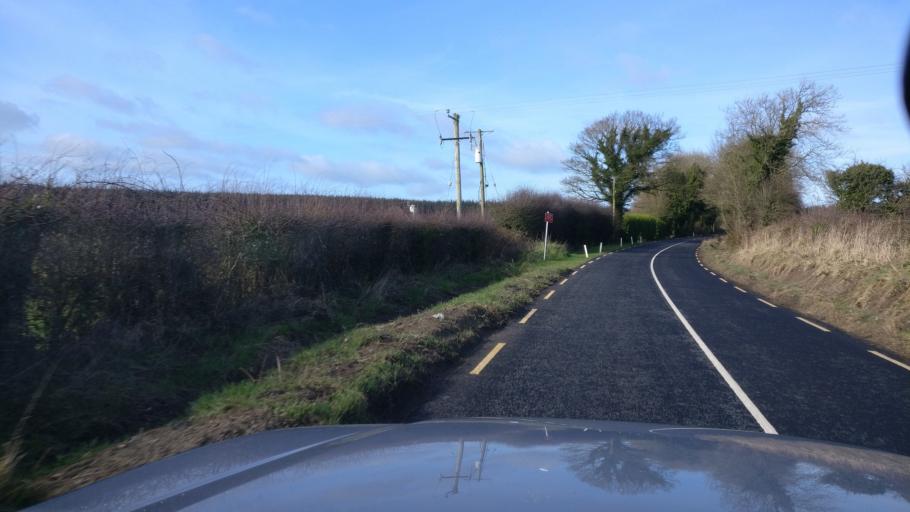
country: IE
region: Leinster
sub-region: Kilkenny
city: Castlecomer
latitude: 52.9063
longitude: -7.1825
